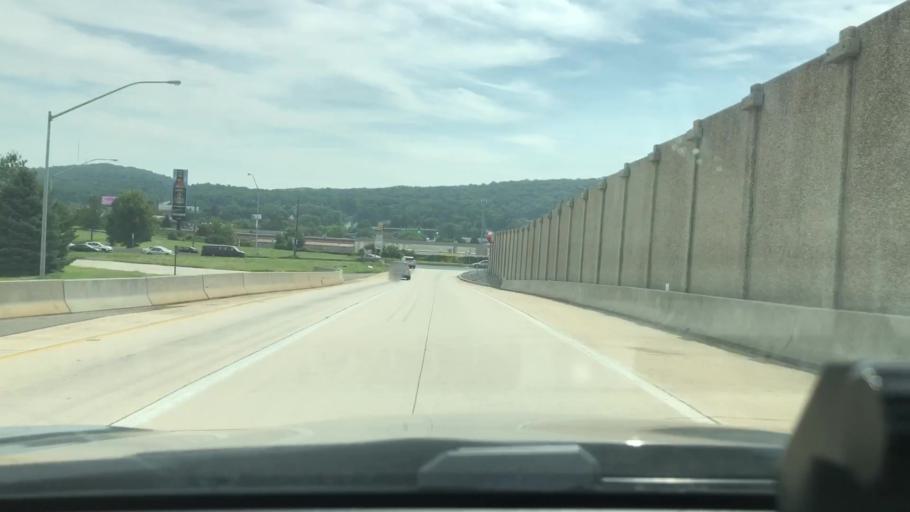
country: US
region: Pennsylvania
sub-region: Lehigh County
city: Emmaus
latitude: 40.5637
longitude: -75.4869
